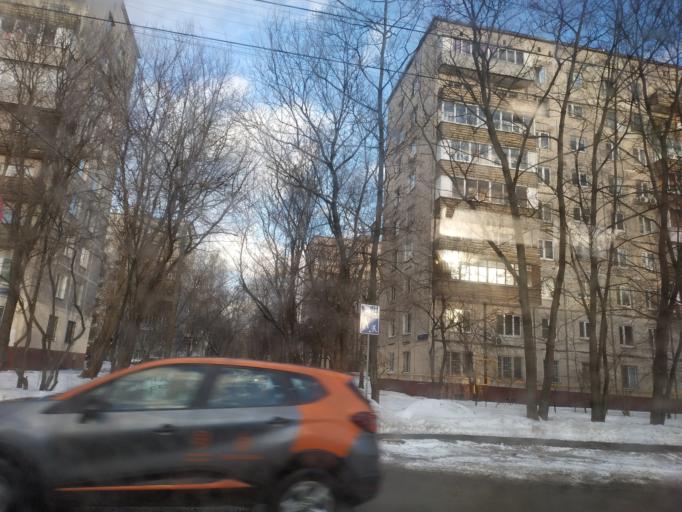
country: RU
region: Moskovskaya
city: Izmaylovo
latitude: 55.8003
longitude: 37.8190
